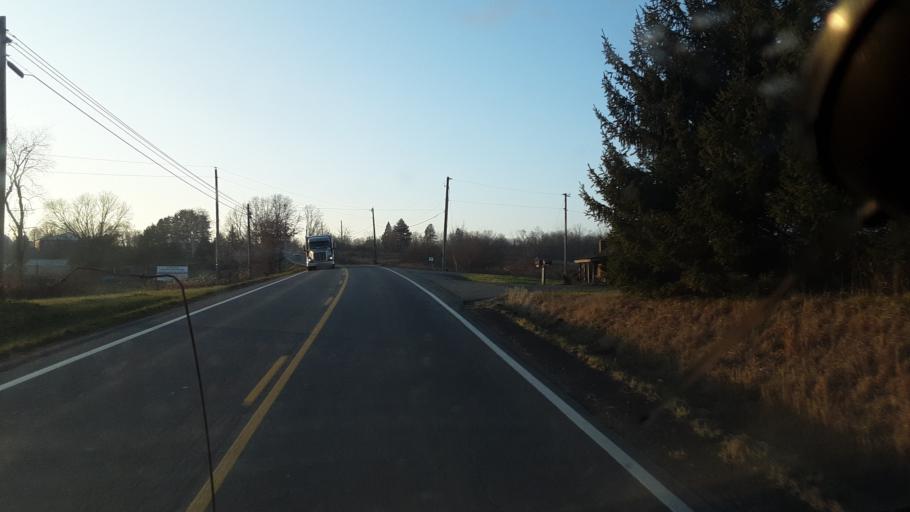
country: US
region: Ohio
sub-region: Knox County
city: Gambier
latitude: 40.4136
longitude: -82.3853
